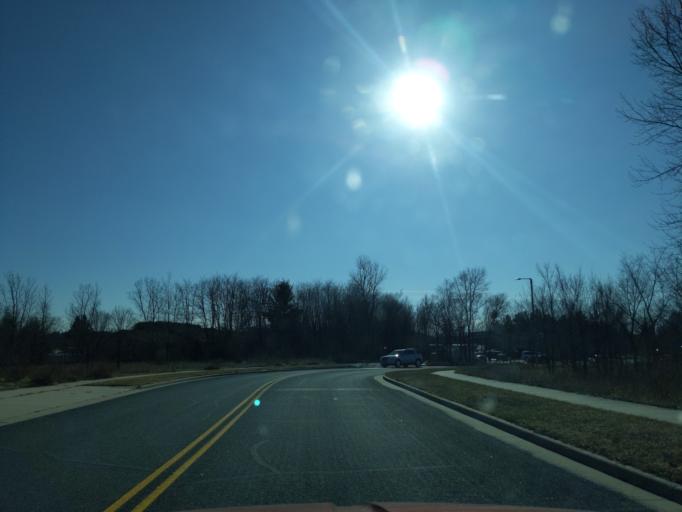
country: US
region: Wisconsin
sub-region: Waushara County
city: Wautoma
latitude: 44.0708
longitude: -89.2674
